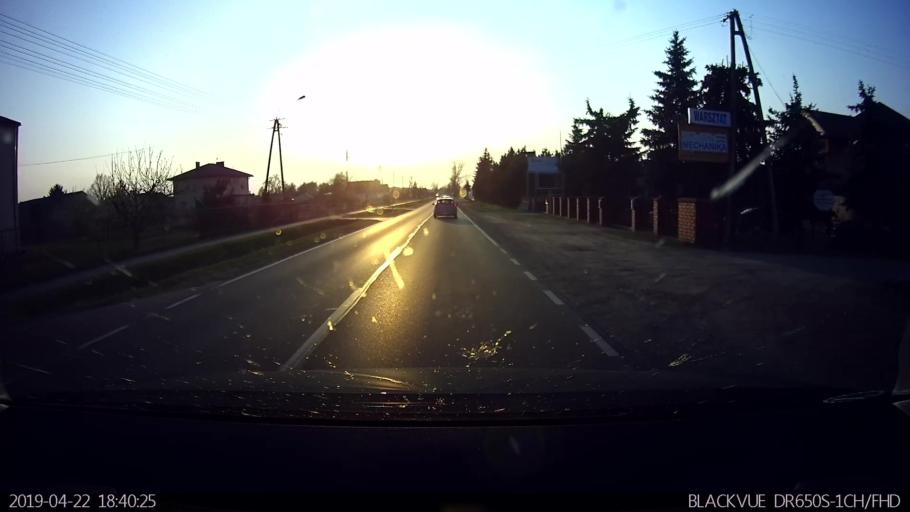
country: PL
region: Masovian Voivodeship
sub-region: Powiat wolominski
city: Dabrowka
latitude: 52.4461
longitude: 21.2772
